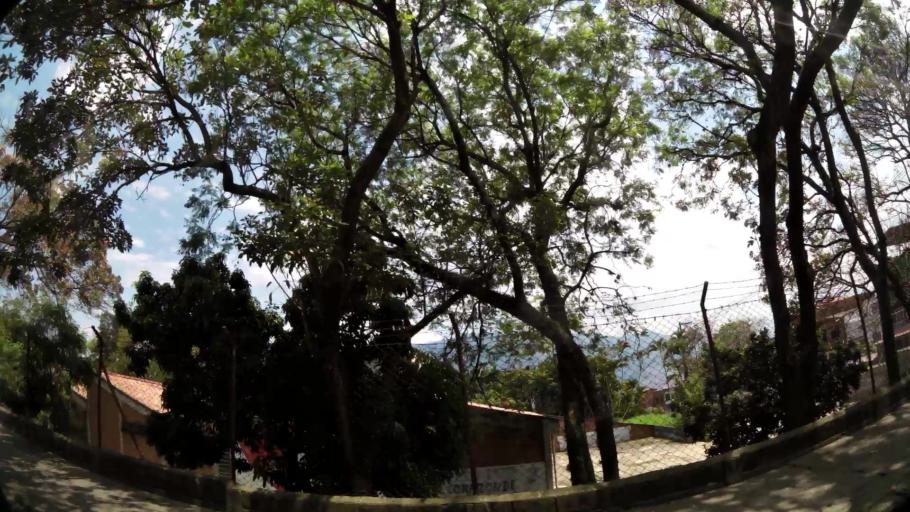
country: CO
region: Antioquia
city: Bello
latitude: 6.2966
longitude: -75.5760
